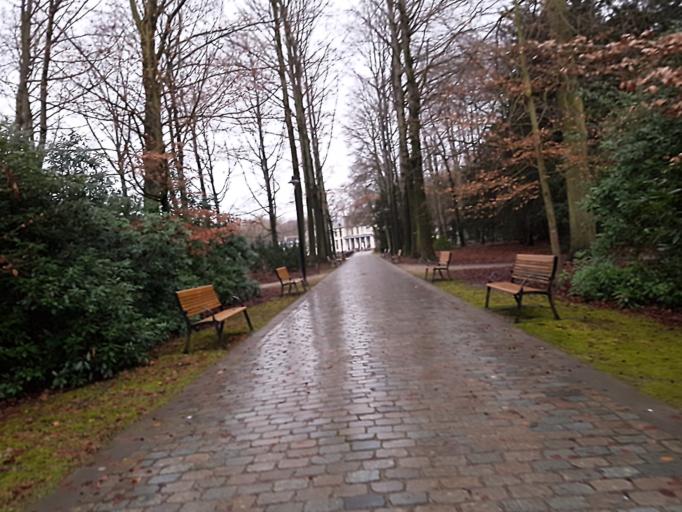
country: BE
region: Flanders
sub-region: Provincie Antwerpen
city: Borsbeek
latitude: 51.2159
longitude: 4.4702
